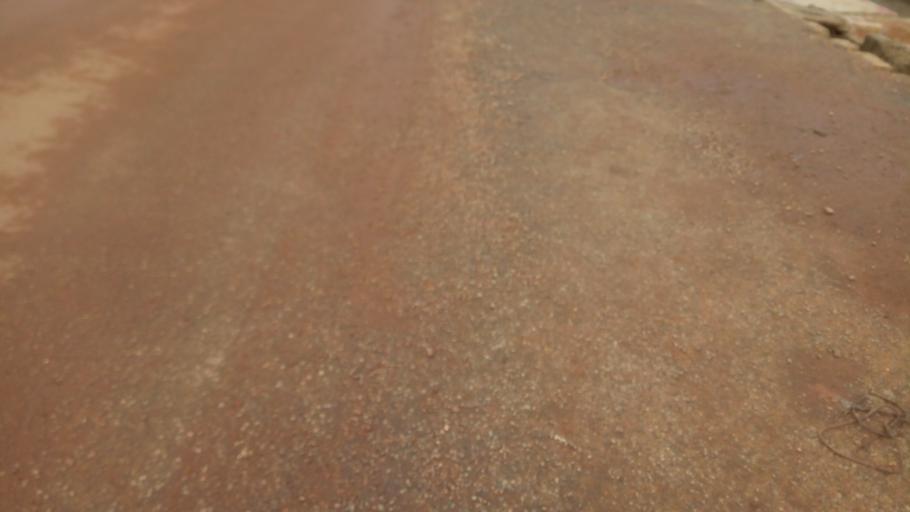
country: GH
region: Ashanti
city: Obuasi
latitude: 6.2111
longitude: -1.6899
